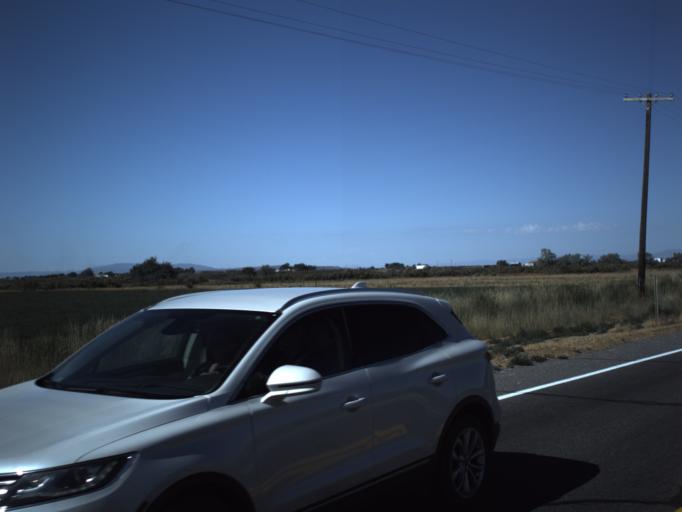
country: US
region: Utah
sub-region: Millard County
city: Delta
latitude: 39.3305
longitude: -112.6161
